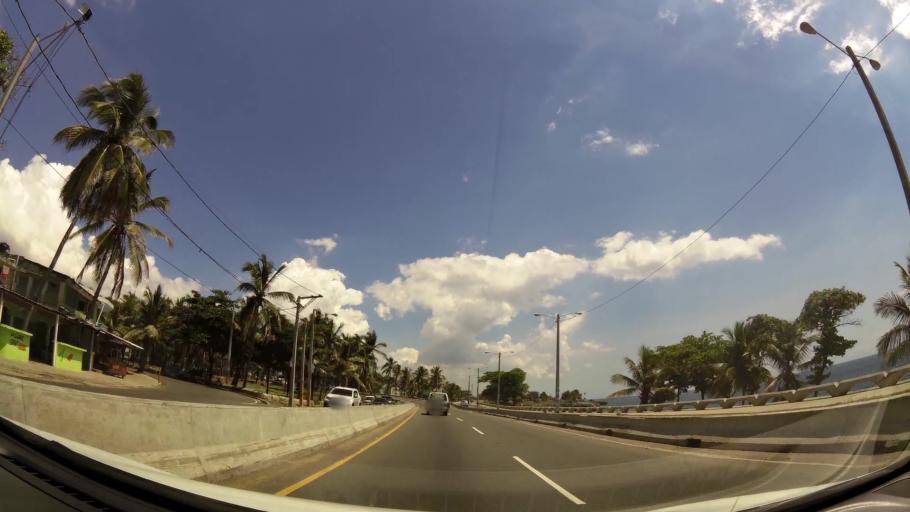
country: DO
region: Santo Domingo
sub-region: Santo Domingo
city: Santo Domingo Este
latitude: 18.4689
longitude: -69.8321
